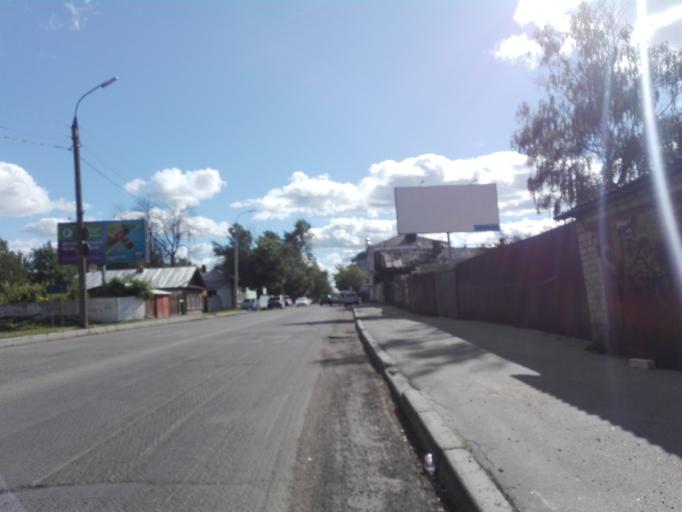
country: RU
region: Orjol
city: Orel
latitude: 52.9608
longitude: 36.0616
